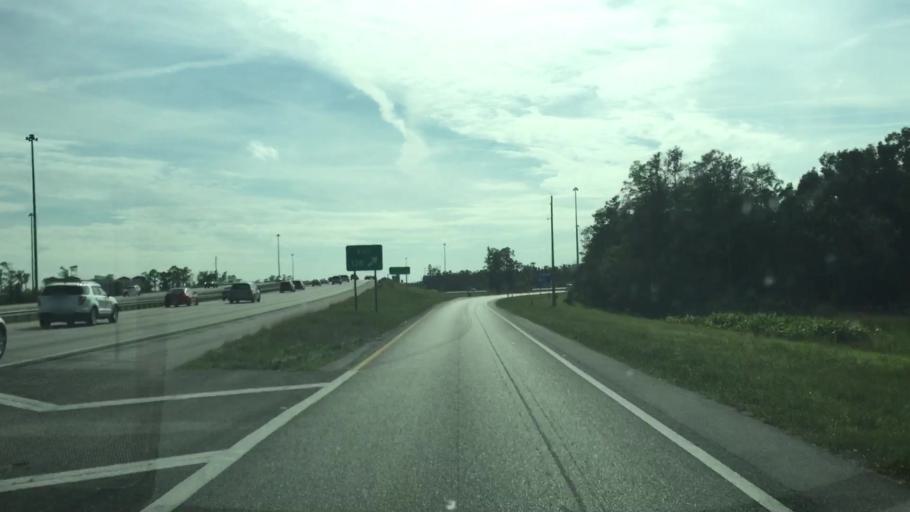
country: US
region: Florida
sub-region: Lee County
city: Tice
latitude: 26.6389
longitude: -81.8020
